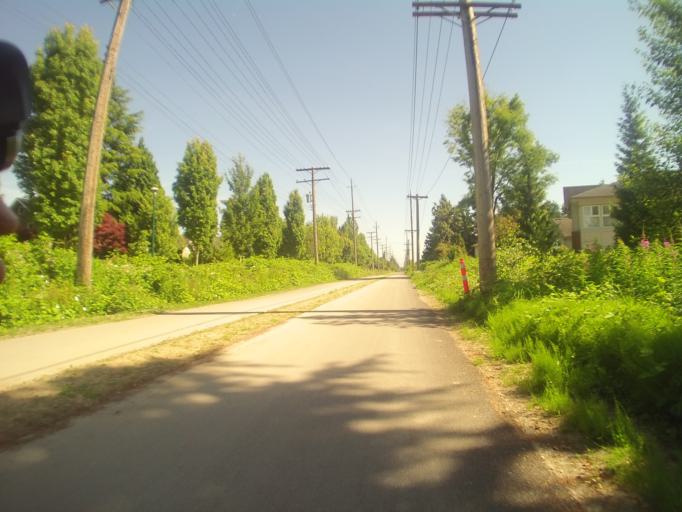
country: CA
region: British Columbia
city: Vancouver
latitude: 49.2268
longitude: -123.1545
